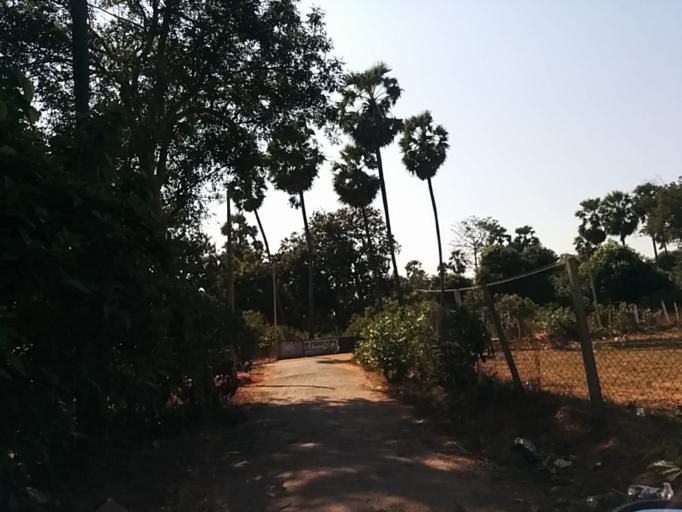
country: IN
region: Pondicherry
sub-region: Puducherry
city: Puducherry
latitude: 11.9627
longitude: 79.8257
